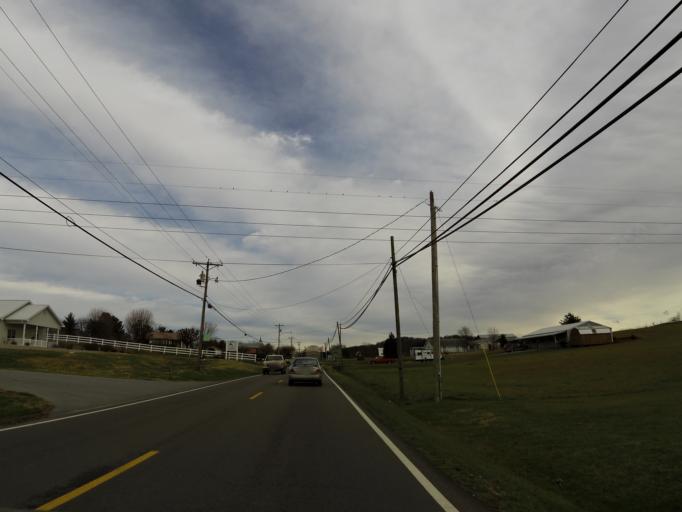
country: US
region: Tennessee
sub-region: Greene County
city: Greeneville
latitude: 36.1406
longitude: -82.8702
